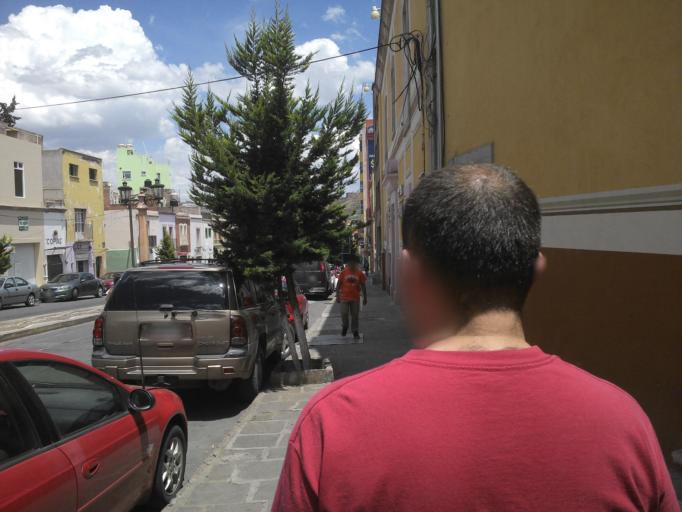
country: MX
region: Zacatecas
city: Zacatecas
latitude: 22.7705
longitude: -102.5706
